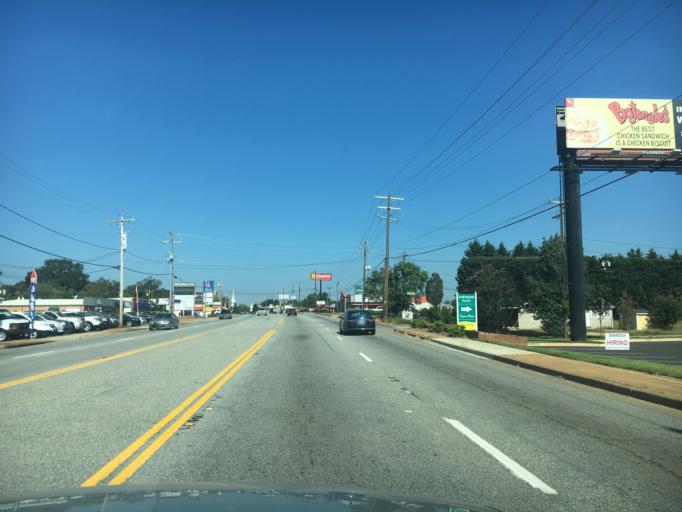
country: US
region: South Carolina
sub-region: Spartanburg County
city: Boiling Springs
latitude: 35.0384
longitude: -81.9739
